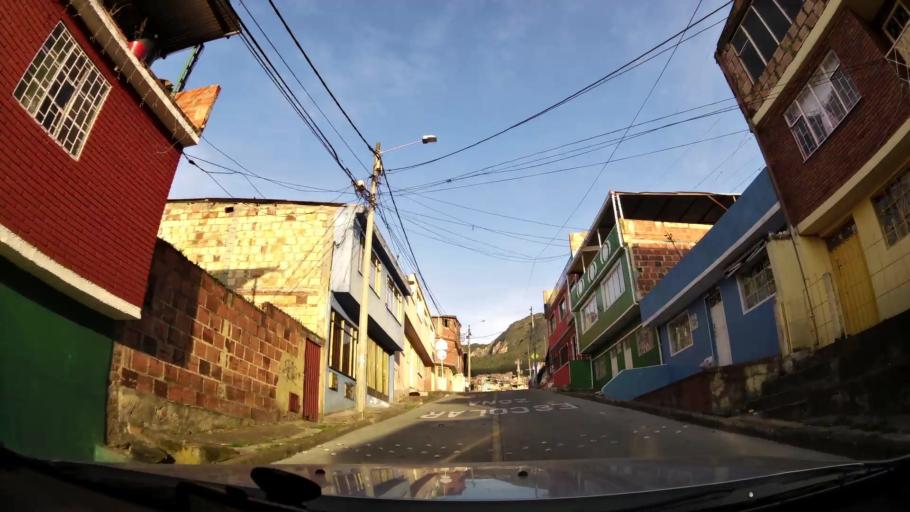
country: CO
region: Bogota D.C.
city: Bogota
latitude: 4.5428
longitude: -74.0869
